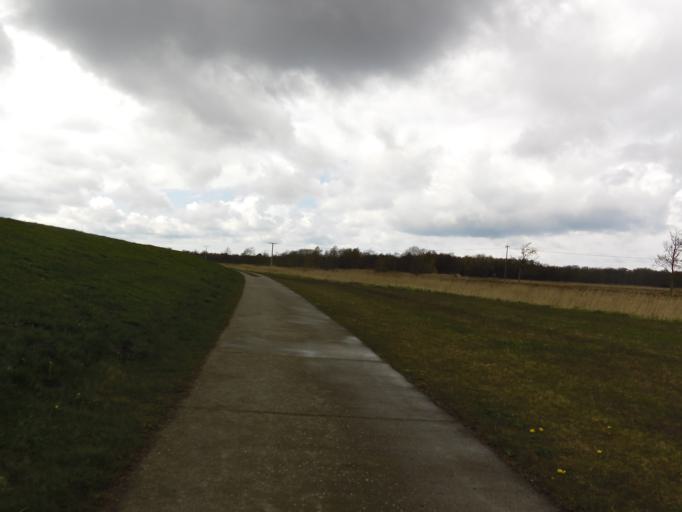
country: DE
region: Mecklenburg-Vorpommern
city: Barth
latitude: 54.4172
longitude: 12.7920
